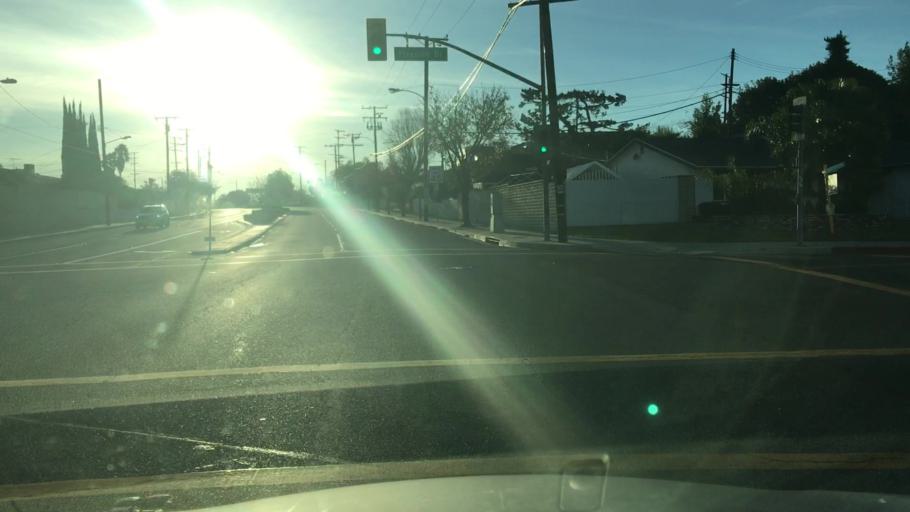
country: US
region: California
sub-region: Los Angeles County
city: East La Mirada
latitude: 33.9259
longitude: -117.9815
